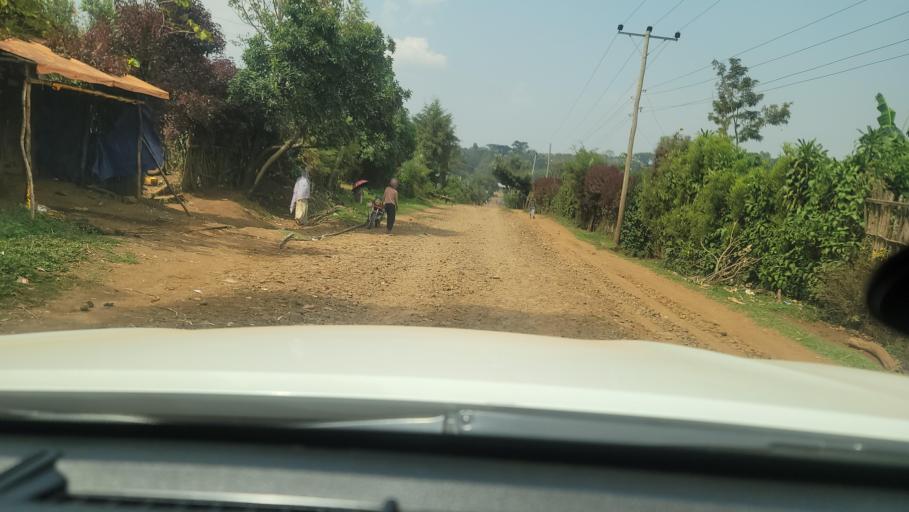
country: ET
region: Oromiya
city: Agaro
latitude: 7.8080
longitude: 36.4690
